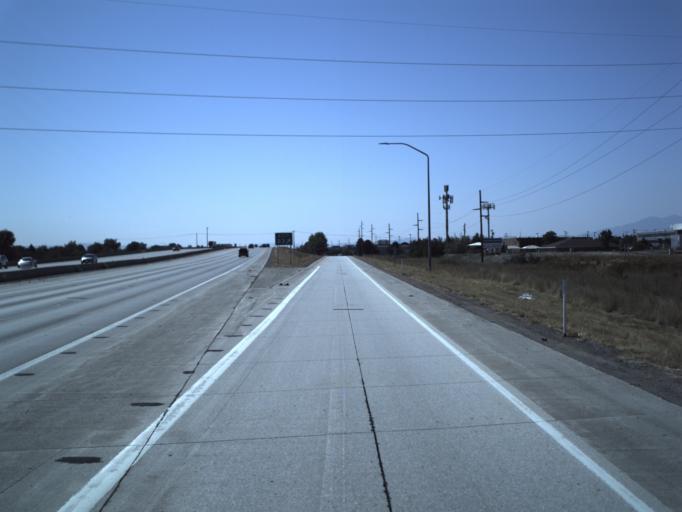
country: US
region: Utah
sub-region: Salt Lake County
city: Salt Lake City
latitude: 40.7904
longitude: -111.9495
